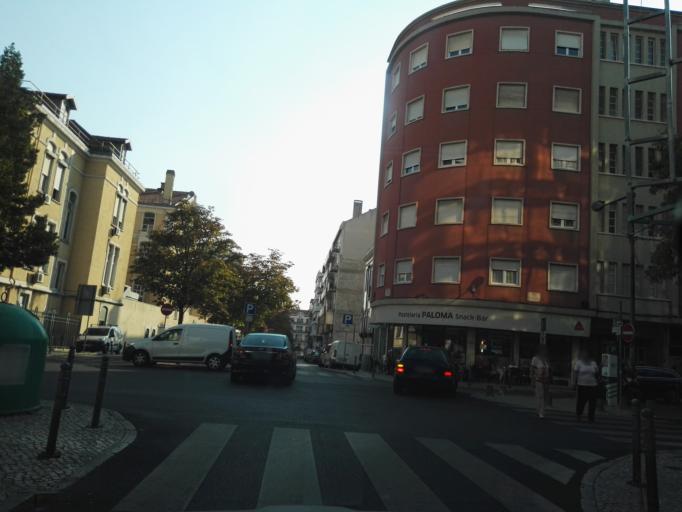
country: PT
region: Lisbon
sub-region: Lisbon
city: Lisbon
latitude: 38.7335
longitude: -9.1476
